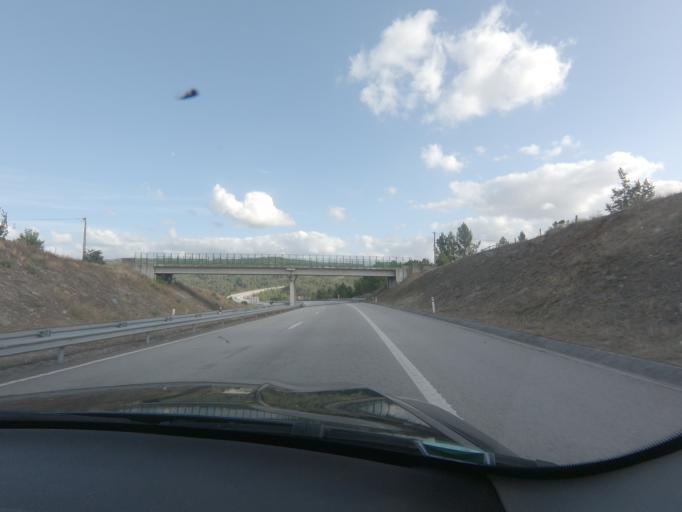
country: PT
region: Viseu
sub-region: Viseu
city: Campo
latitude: 40.8034
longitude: -7.9319
